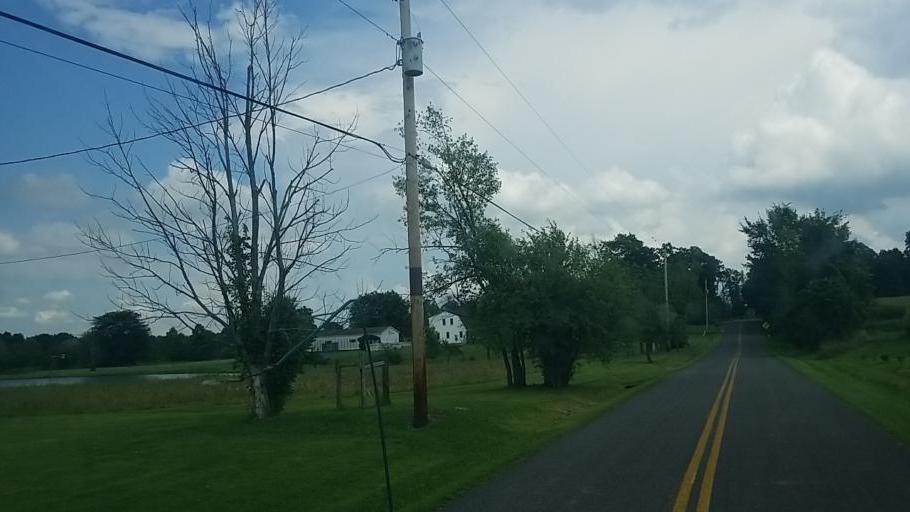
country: US
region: Ohio
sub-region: Medina County
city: Lodi
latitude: 41.1433
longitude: -81.9882
